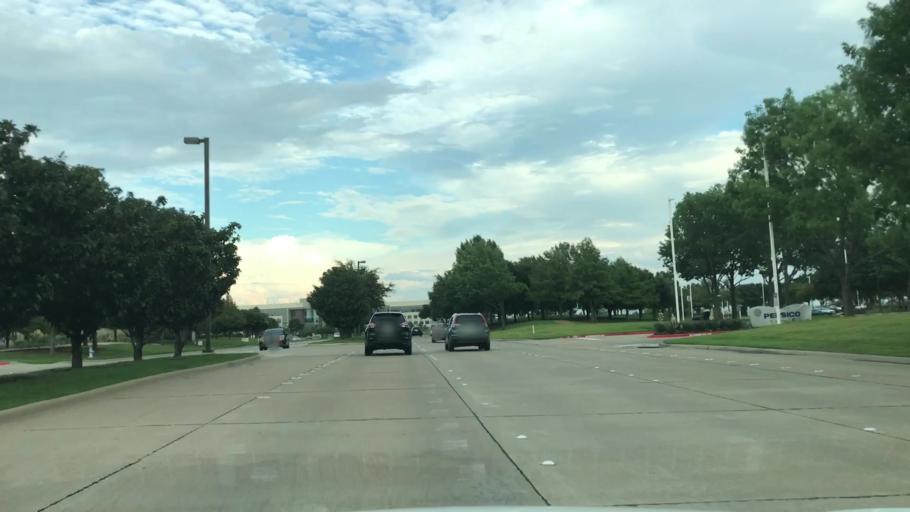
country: US
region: Texas
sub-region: Collin County
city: Frisco
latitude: 33.0840
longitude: -96.8161
